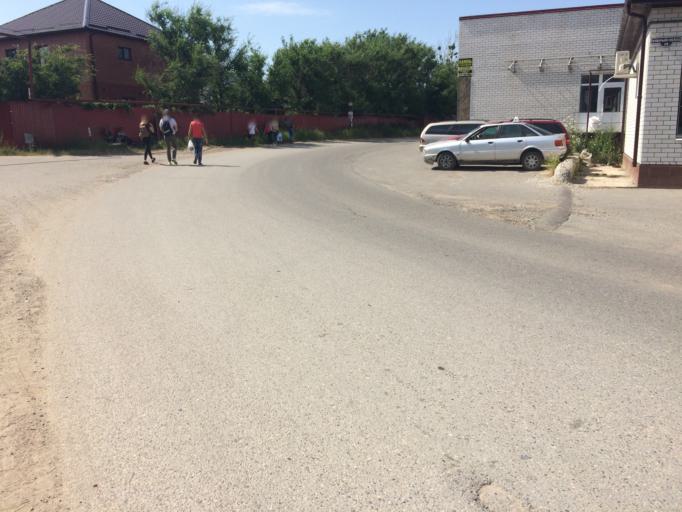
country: RU
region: Stavropol'skiy
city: Tatarka
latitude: 44.9895
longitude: 41.9371
